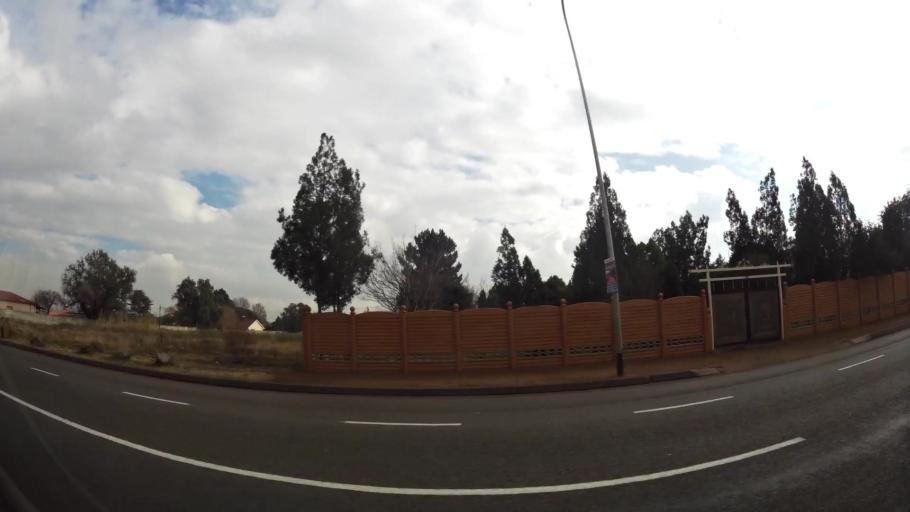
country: ZA
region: Gauteng
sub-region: Sedibeng District Municipality
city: Meyerton
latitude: -26.5952
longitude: 27.9927
